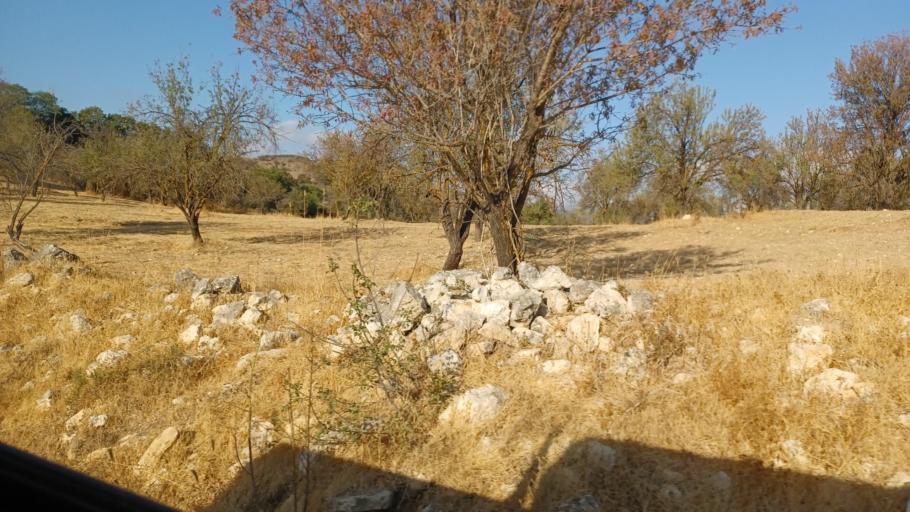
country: CY
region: Pafos
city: Tala
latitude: 34.9269
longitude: 32.4949
